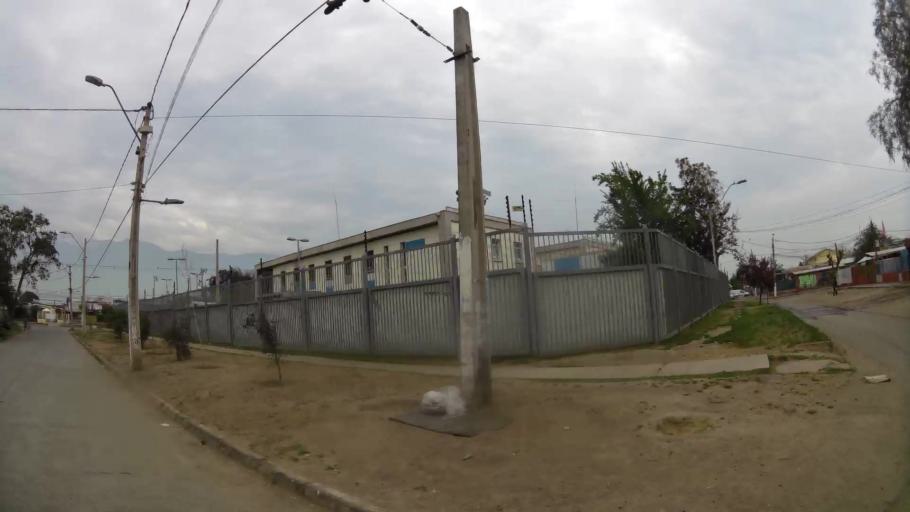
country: CL
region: Santiago Metropolitan
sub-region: Provincia de Santiago
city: Villa Presidente Frei, Nunoa, Santiago, Chile
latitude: -33.4760
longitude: -70.5932
